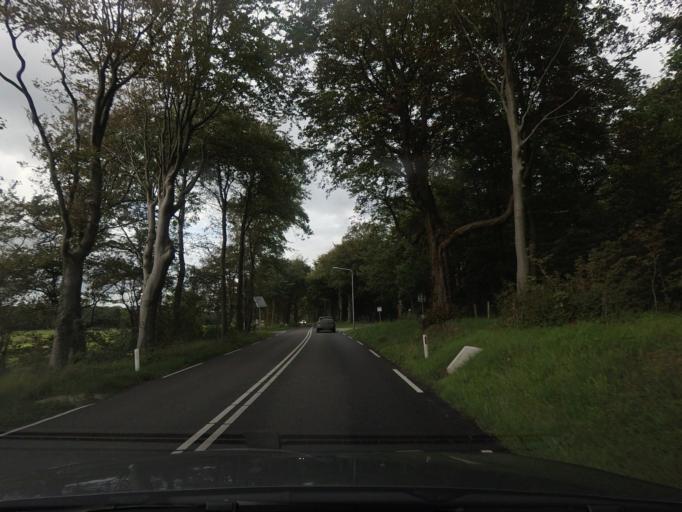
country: NL
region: North Holland
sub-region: Gemeente Bloemendaal
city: Bennebroek
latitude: 52.3374
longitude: 4.5825
